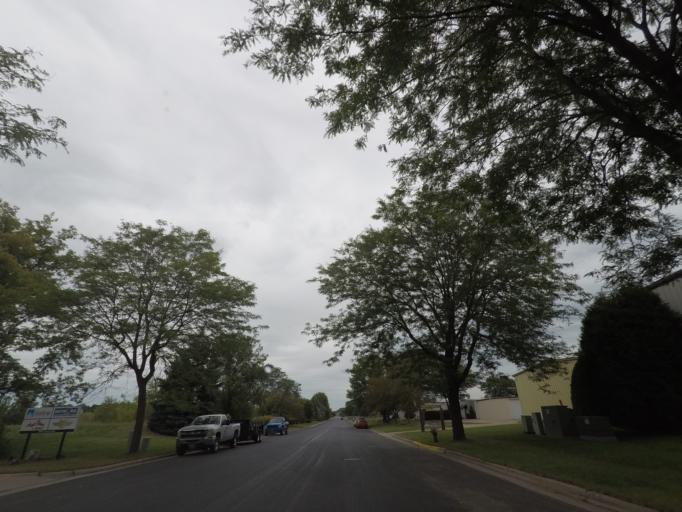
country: US
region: Wisconsin
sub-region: Dane County
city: Middleton
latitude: 43.1076
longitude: -89.5144
